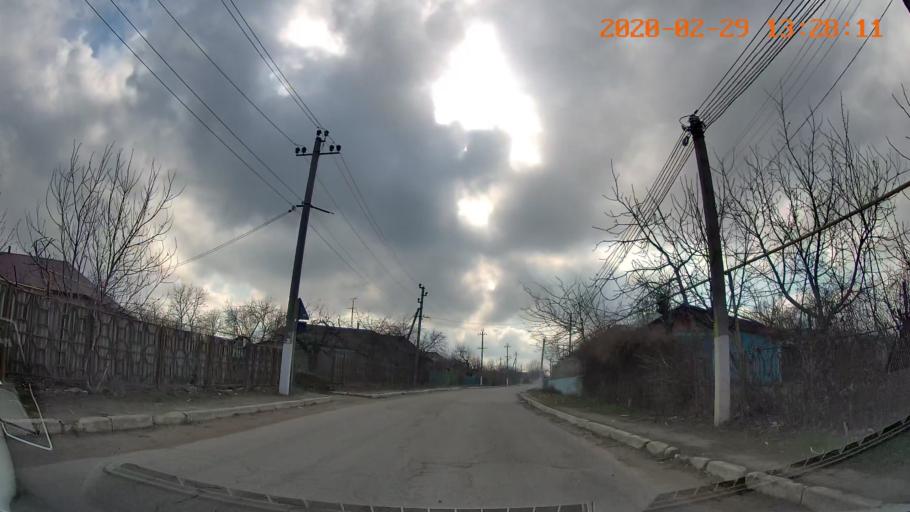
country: MD
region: Telenesti
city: Camenca
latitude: 47.9076
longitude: 28.6437
